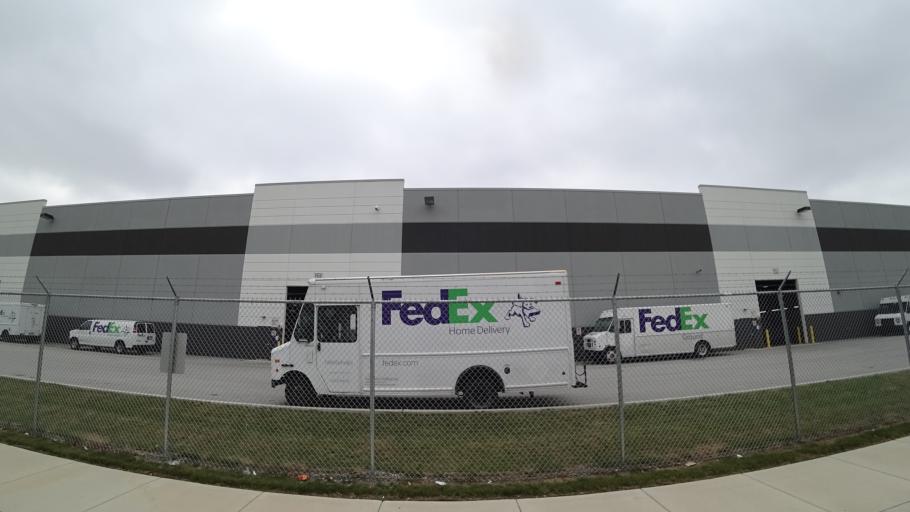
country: US
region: Illinois
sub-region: Cook County
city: Chicago
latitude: 41.8395
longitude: -87.6731
